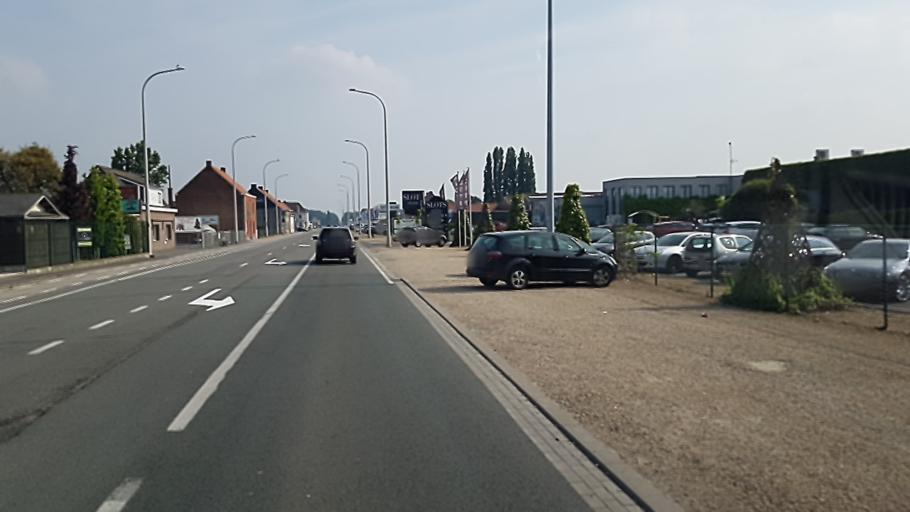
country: BE
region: Wallonia
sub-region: Province du Hainaut
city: Pecq
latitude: 50.7287
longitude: 3.3297
